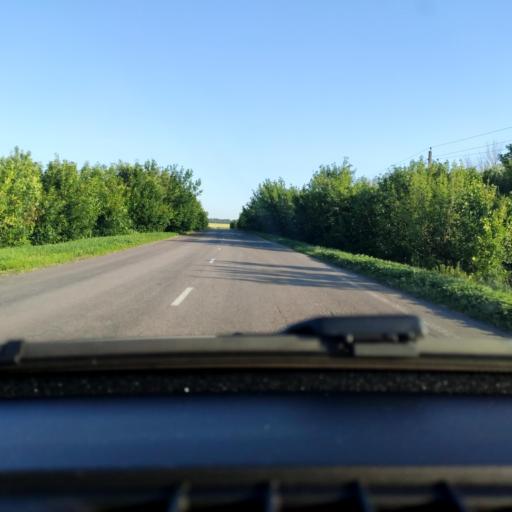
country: RU
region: Voronezj
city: Kashirskoye
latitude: 51.5044
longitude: 39.8321
